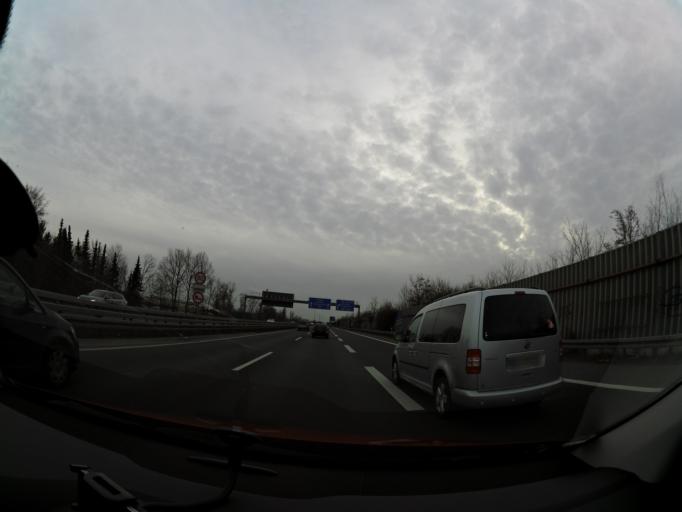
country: DE
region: Lower Saxony
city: Braunschweig
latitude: 52.2780
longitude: 10.4918
